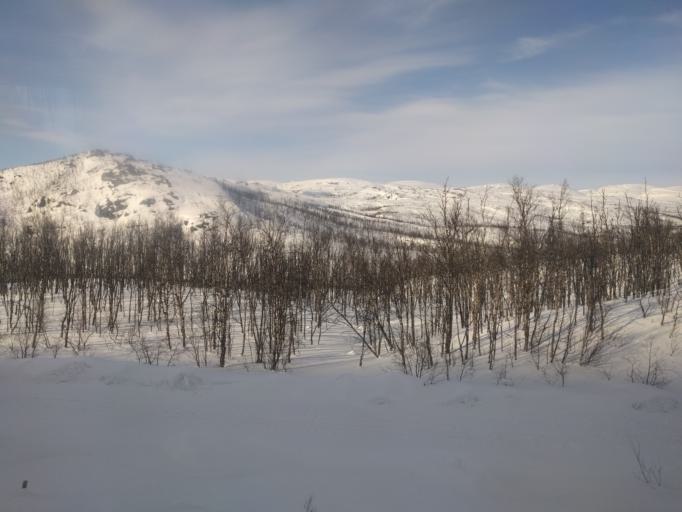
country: NO
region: Troms
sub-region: Bardu
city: Setermoen
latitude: 68.4253
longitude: 18.4402
